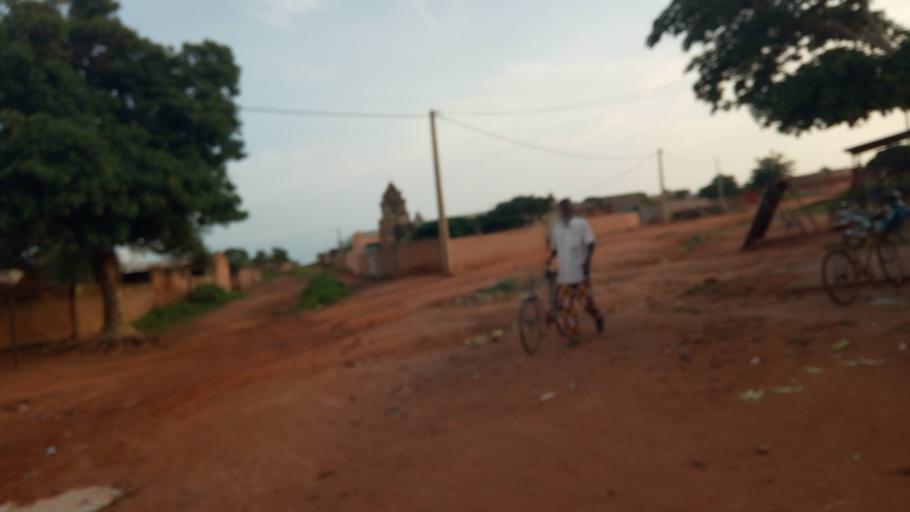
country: ML
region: Sikasso
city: Koutiala
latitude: 12.3750
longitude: -5.4916
